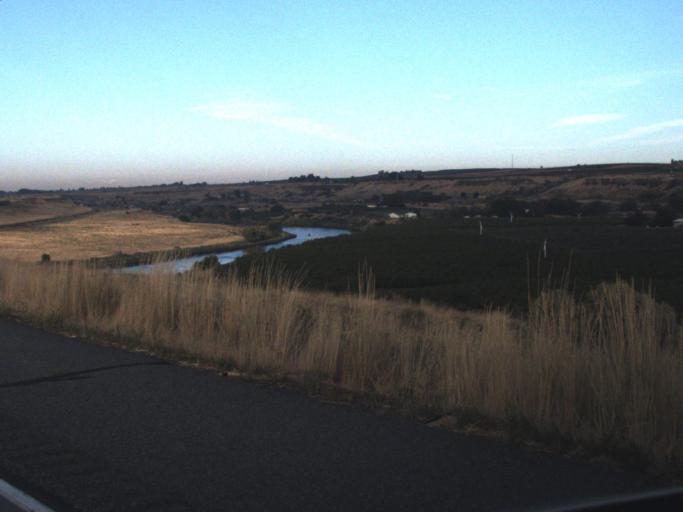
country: US
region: Washington
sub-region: Benton County
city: Benton City
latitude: 46.2556
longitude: -119.5973
